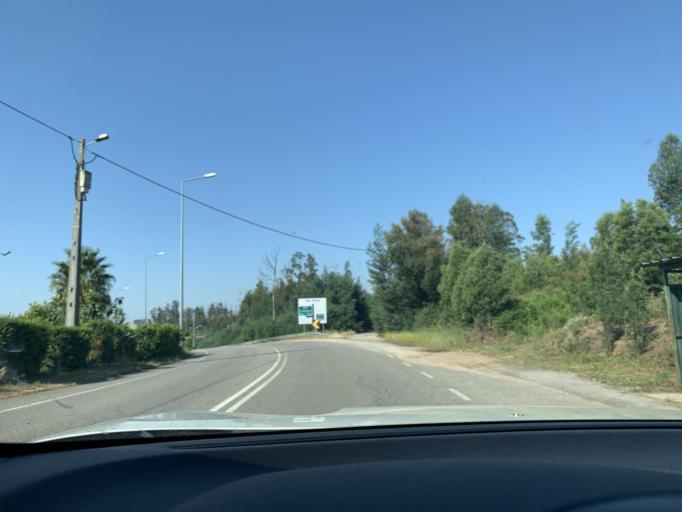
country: PT
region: Viseu
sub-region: Santa Comba Dao
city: Santa Comba Dao
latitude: 40.4387
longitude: -8.1072
